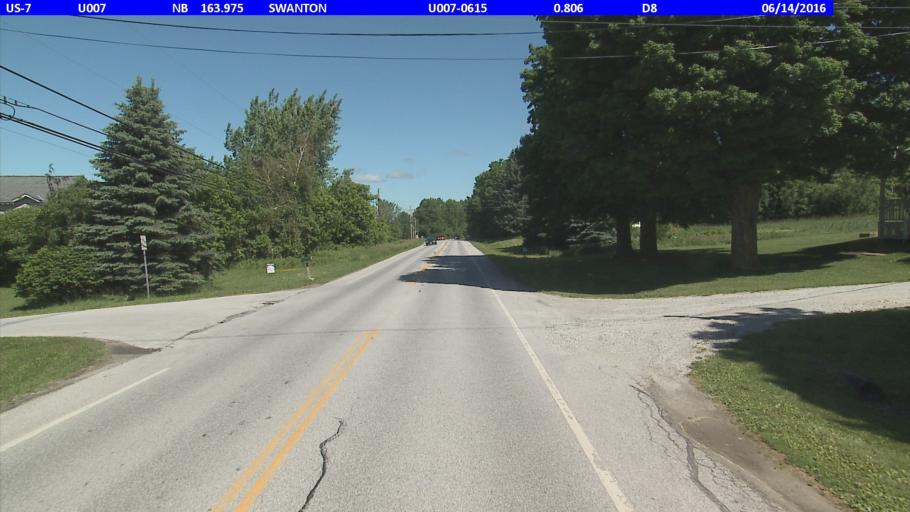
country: US
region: Vermont
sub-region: Franklin County
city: Saint Albans
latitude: 44.8596
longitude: -73.0957
